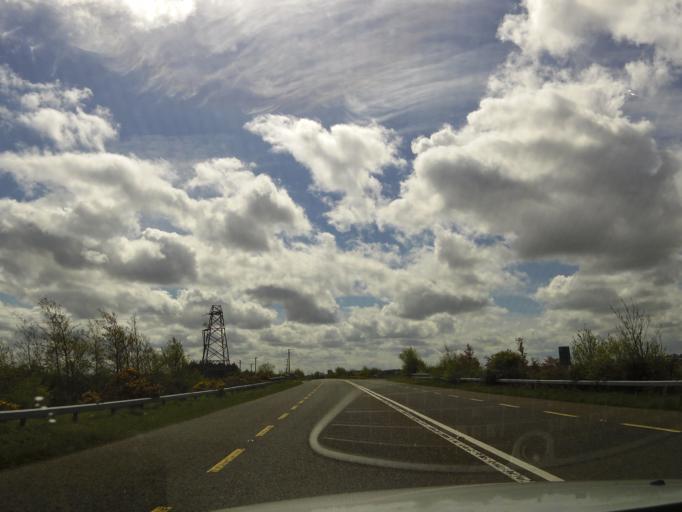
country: IE
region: Connaught
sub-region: Maigh Eo
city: Claremorris
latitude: 53.7194
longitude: -8.9854
